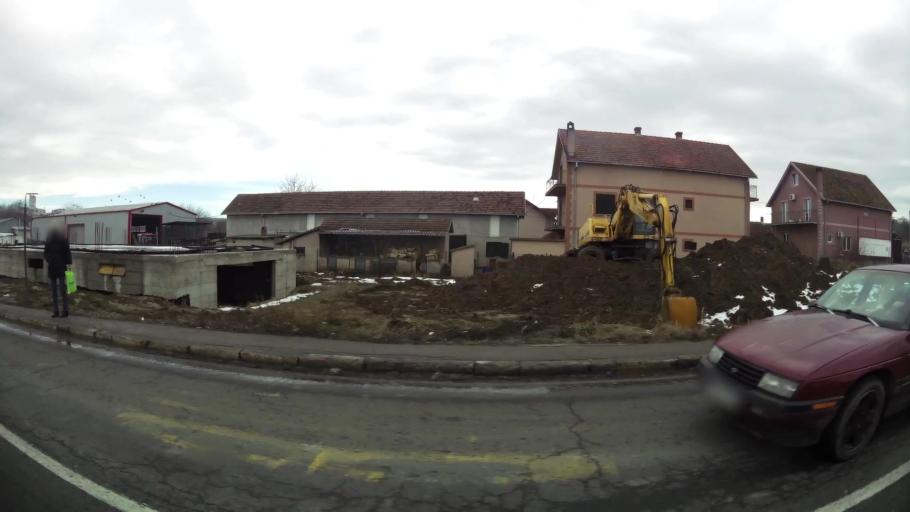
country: RS
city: Ostruznica
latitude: 44.7229
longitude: 20.3686
